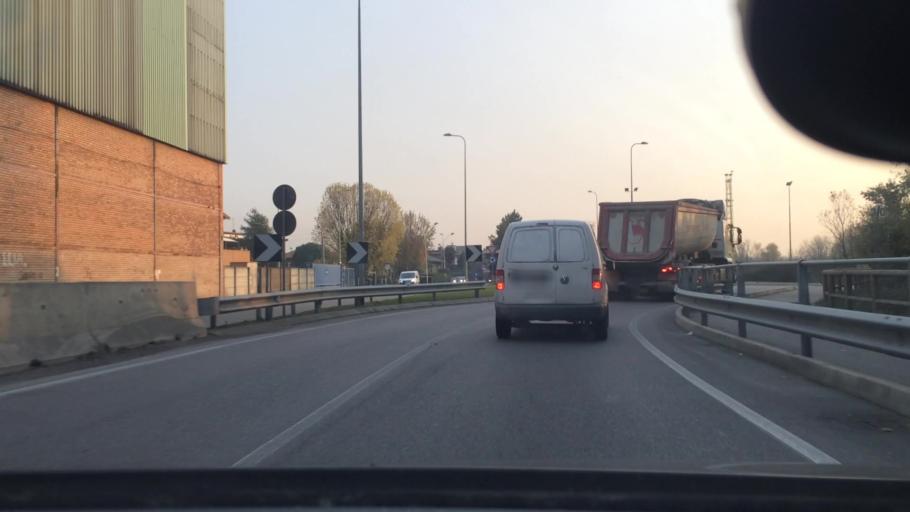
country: IT
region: Lombardy
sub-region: Provincia di Monza e Brianza
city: Villaggio del Sole
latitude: 45.6246
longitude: 9.1021
